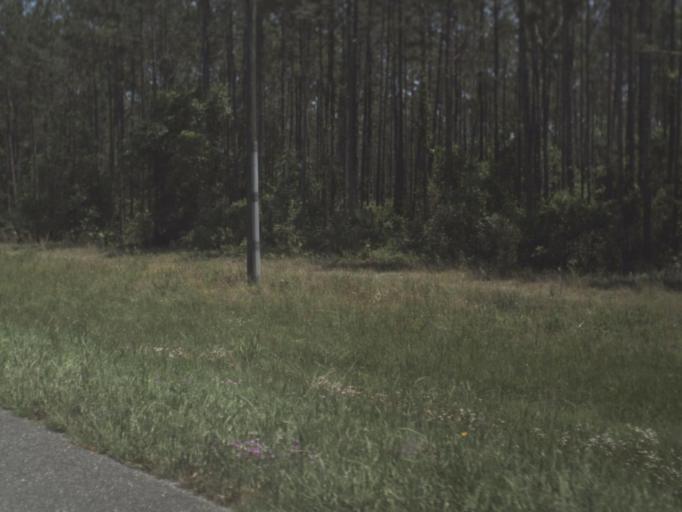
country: US
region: Florida
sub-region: Columbia County
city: Watertown
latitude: 30.1884
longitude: -82.5484
